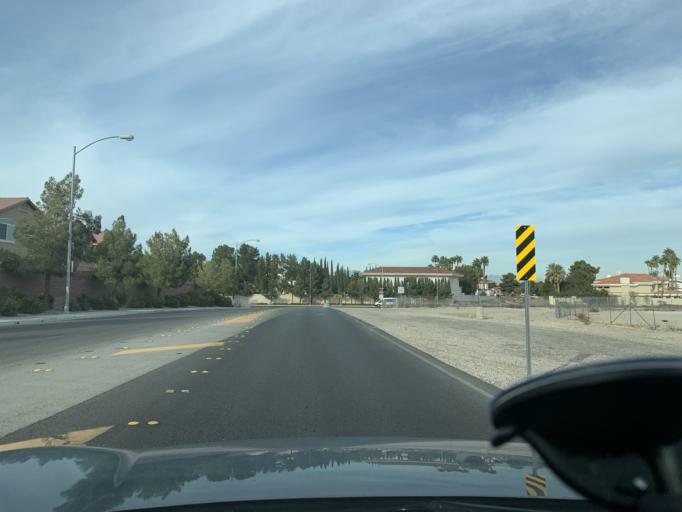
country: US
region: Nevada
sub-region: Clark County
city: Spring Valley
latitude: 36.0911
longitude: -115.2610
